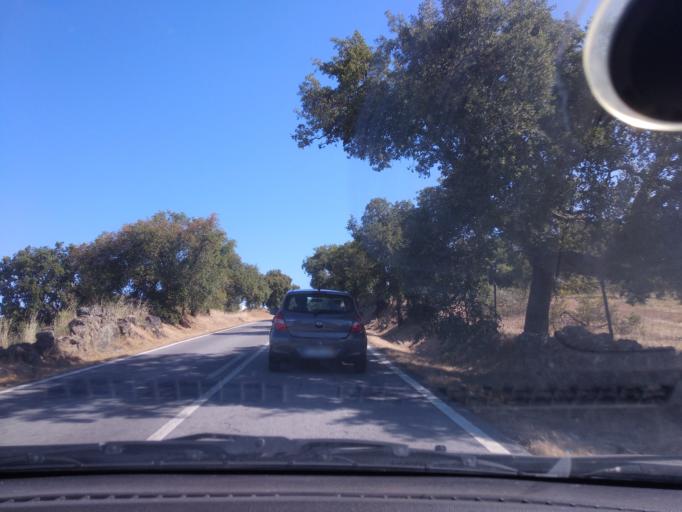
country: PT
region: Portalegre
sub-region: Nisa
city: Nisa
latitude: 39.5033
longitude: -7.6437
